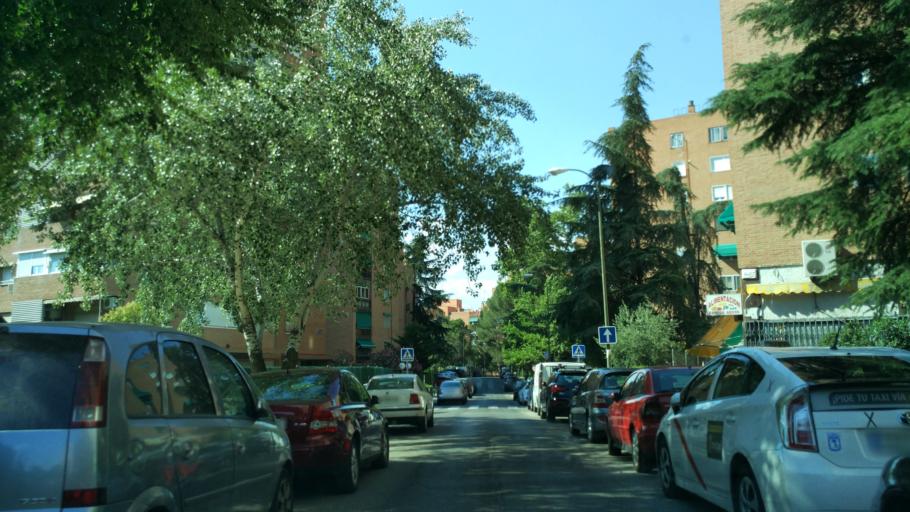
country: ES
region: Madrid
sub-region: Provincia de Madrid
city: Tetuan de las Victorias
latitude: 40.4660
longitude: -3.7213
